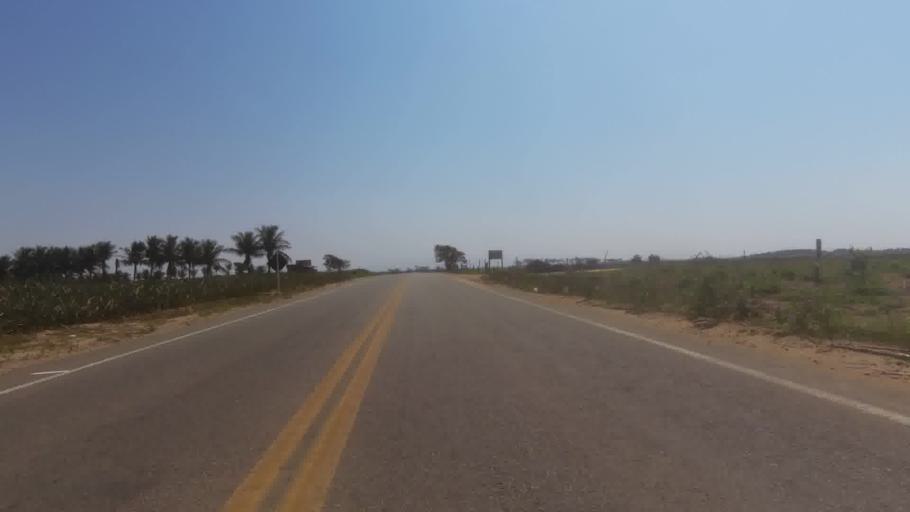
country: BR
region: Espirito Santo
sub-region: Marataizes
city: Marataizes
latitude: -21.0795
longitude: -40.8493
